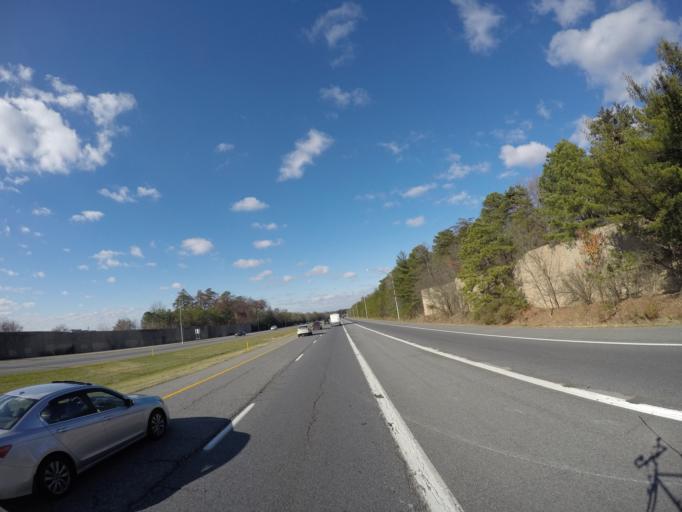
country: US
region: Maryland
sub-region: Anne Arundel County
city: Pasadena
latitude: 39.1369
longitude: -76.5906
